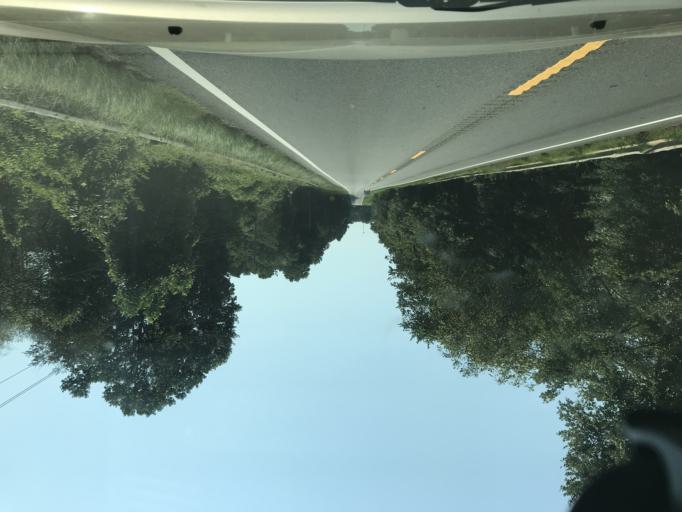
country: US
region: Georgia
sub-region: Hall County
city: Flowery Branch
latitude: 34.2493
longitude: -84.0122
